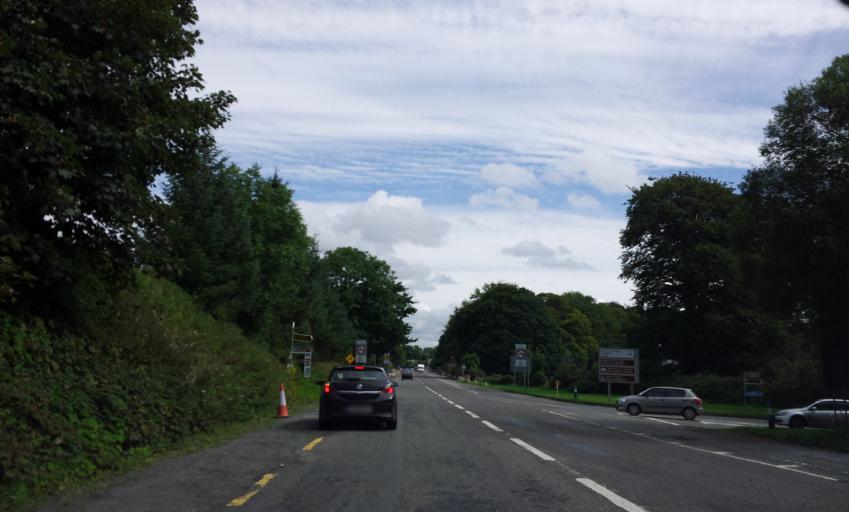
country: IE
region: Munster
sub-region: Ciarrai
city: Cill Airne
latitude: 52.0716
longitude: -9.5947
